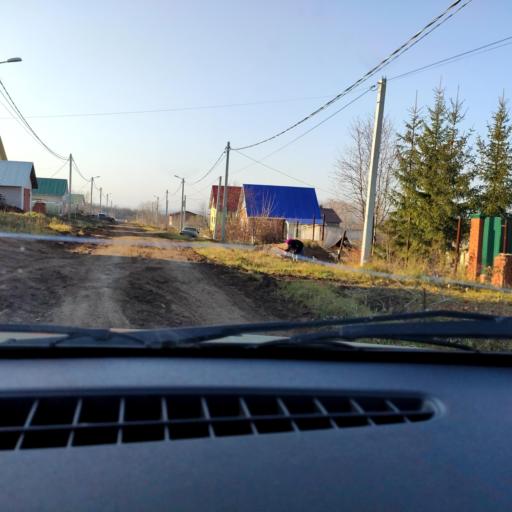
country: RU
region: Bashkortostan
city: Kabakovo
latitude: 54.6289
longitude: 56.0689
